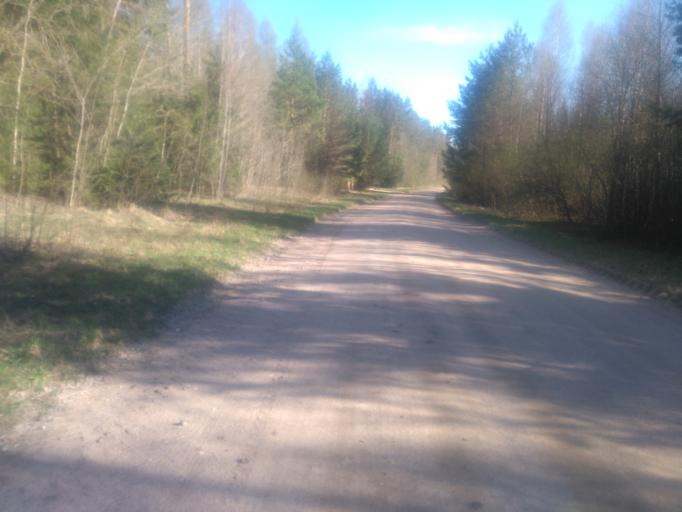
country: LV
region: Vecpiebalga
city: Vecpiebalga
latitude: 57.0117
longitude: 25.8395
